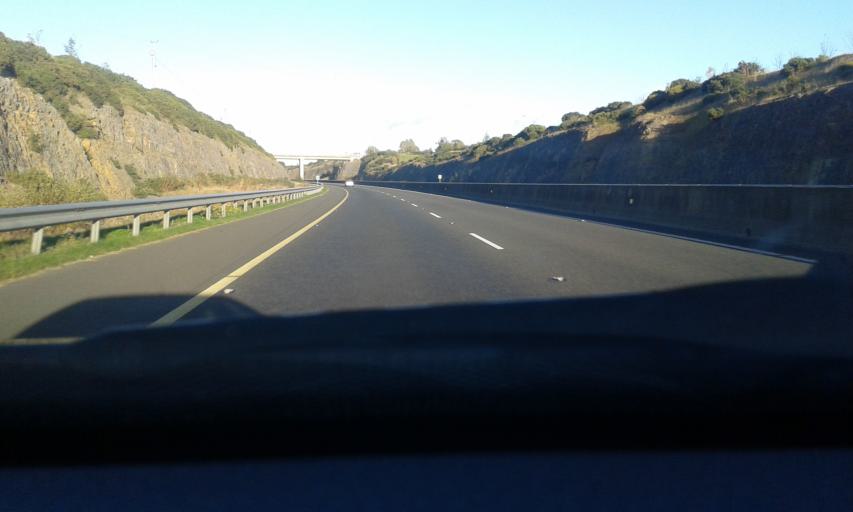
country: IE
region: Leinster
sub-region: Laois
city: Rathdowney
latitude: 52.7599
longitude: -7.5618
